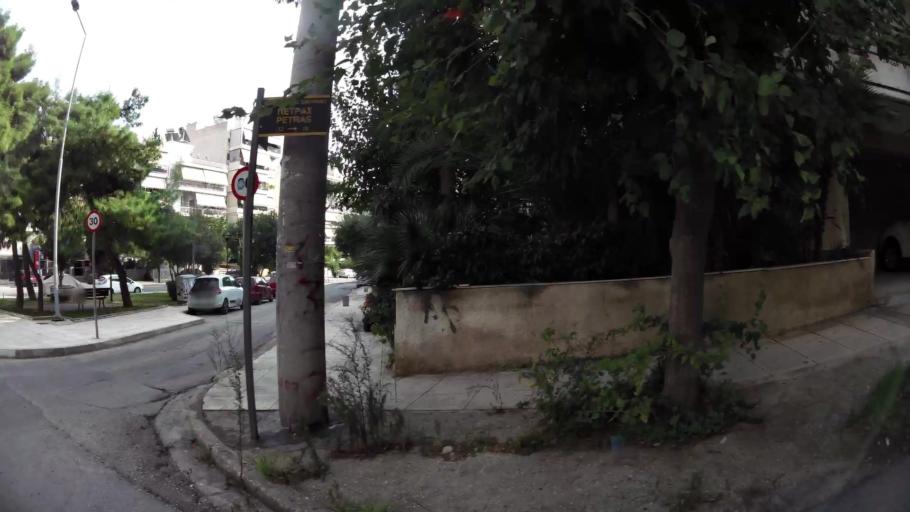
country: GR
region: Attica
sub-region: Nomarchia Athinas
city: Nea Smyrni
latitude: 37.9420
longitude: 23.7230
